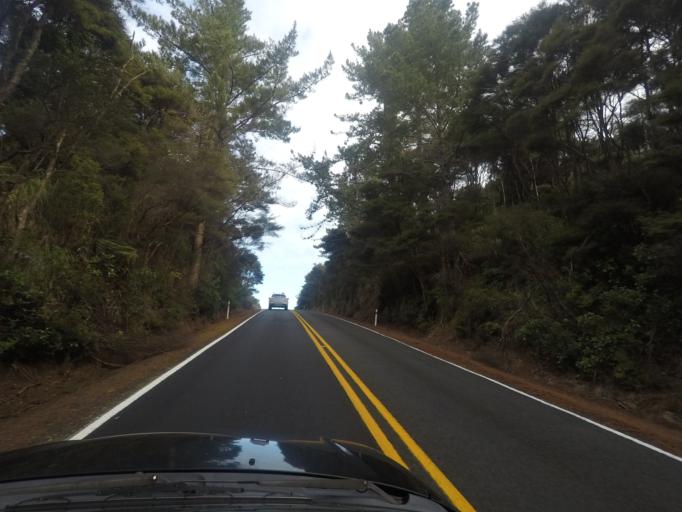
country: NZ
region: Auckland
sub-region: Auckland
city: Titirangi
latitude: -37.0011
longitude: 174.5874
